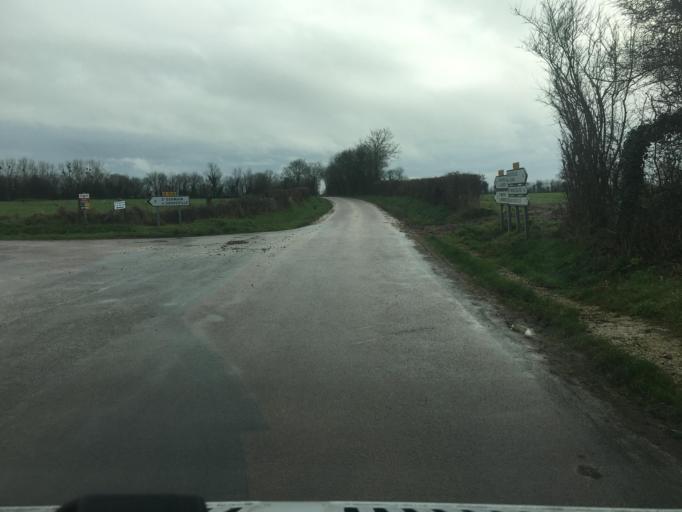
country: FR
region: Lower Normandy
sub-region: Departement de la Manche
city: Sainte-Mere-Eglise
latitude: 49.4204
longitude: -1.2767
